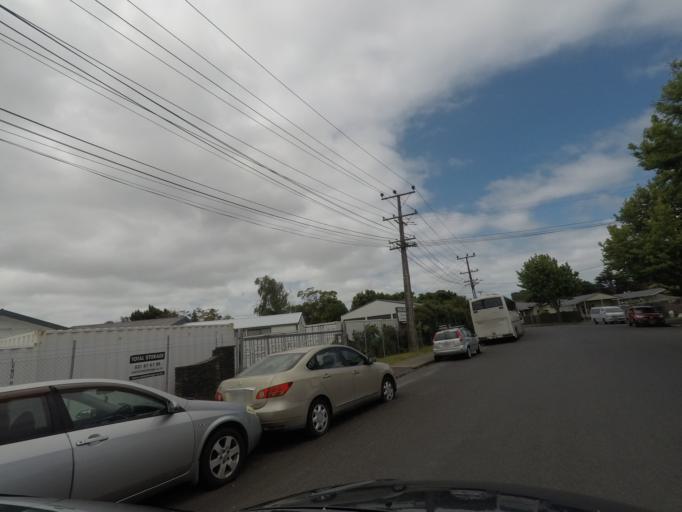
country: NZ
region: Auckland
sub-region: Auckland
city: Waitakere
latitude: -36.9081
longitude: 174.6370
